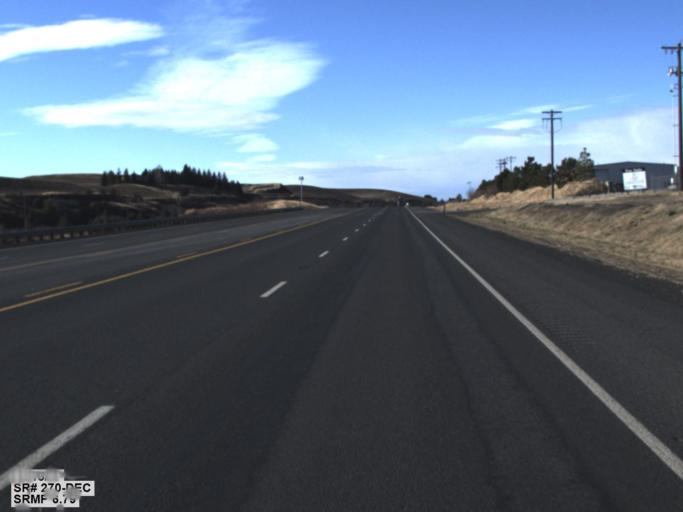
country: US
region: Washington
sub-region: Whitman County
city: Pullman
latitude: 46.7291
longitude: -117.0991
